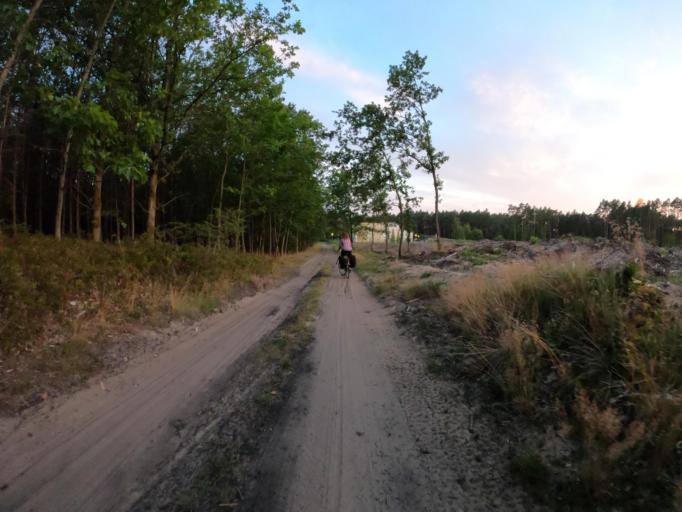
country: PL
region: West Pomeranian Voivodeship
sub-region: Powiat koszalinski
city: Sianow
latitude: 54.0802
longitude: 16.3981
